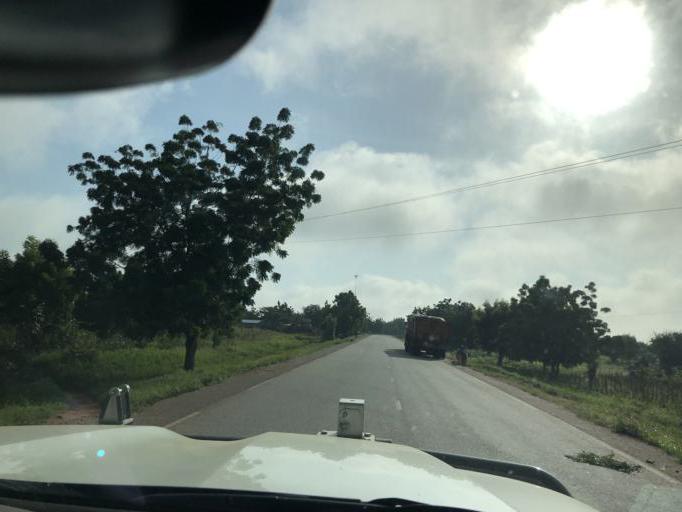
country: CM
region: North Province
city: Pitoa
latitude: 9.4942
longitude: 13.6912
